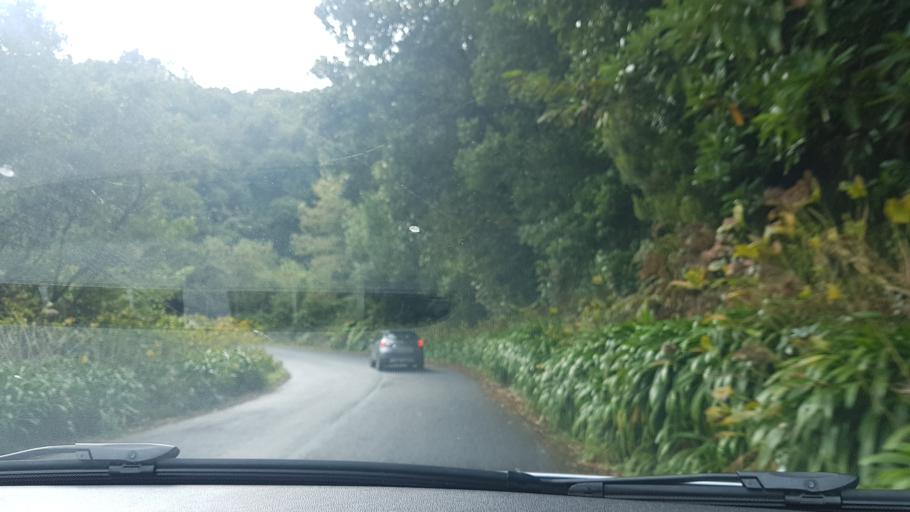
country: PT
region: Madeira
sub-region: Sao Vicente
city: Sao Vicente
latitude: 32.7634
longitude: -17.0222
